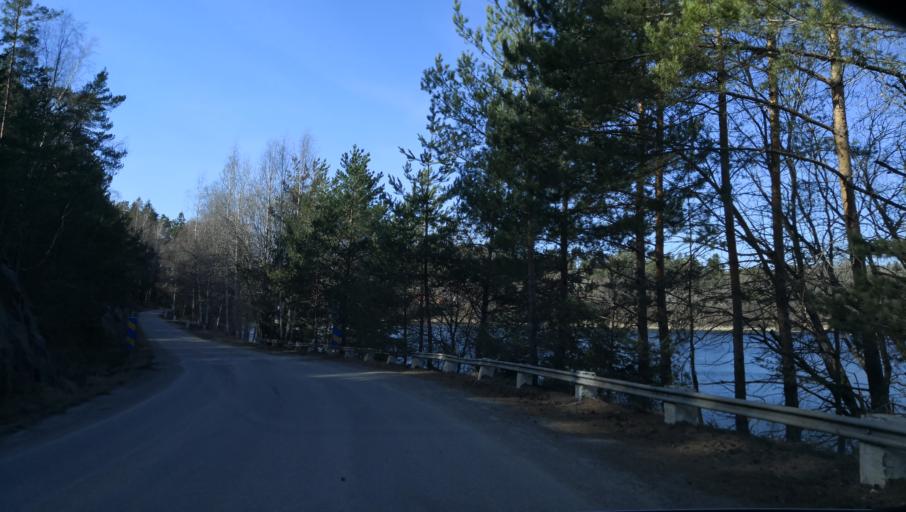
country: SE
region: Stockholm
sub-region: Varmdo Kommun
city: Mortnas
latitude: 59.2965
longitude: 18.4182
